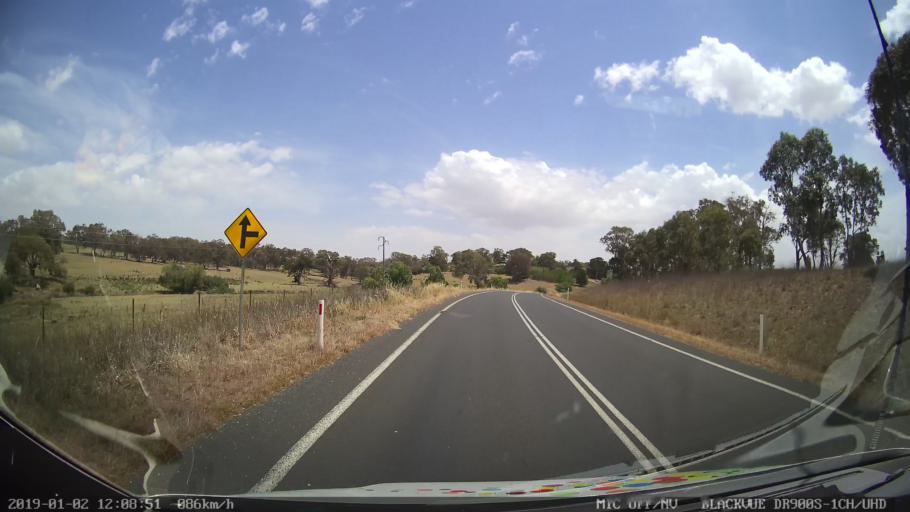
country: AU
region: New South Wales
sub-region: Young
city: Young
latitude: -34.4791
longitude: 148.2732
